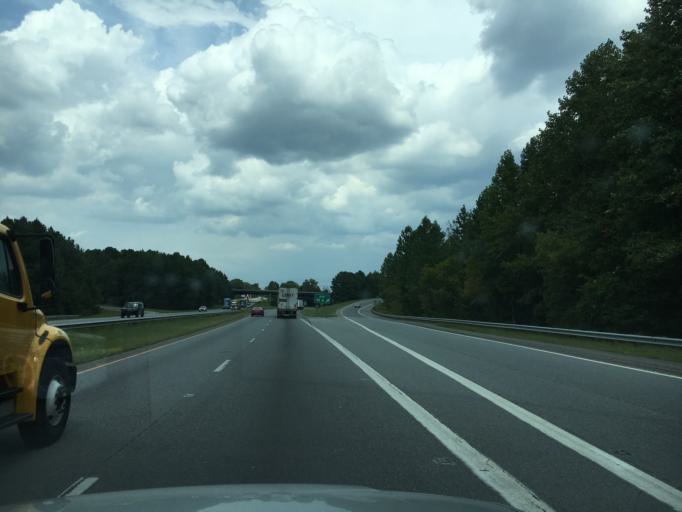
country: US
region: North Carolina
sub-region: Cleveland County
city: Kings Mountain
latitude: 35.2389
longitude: -81.3121
